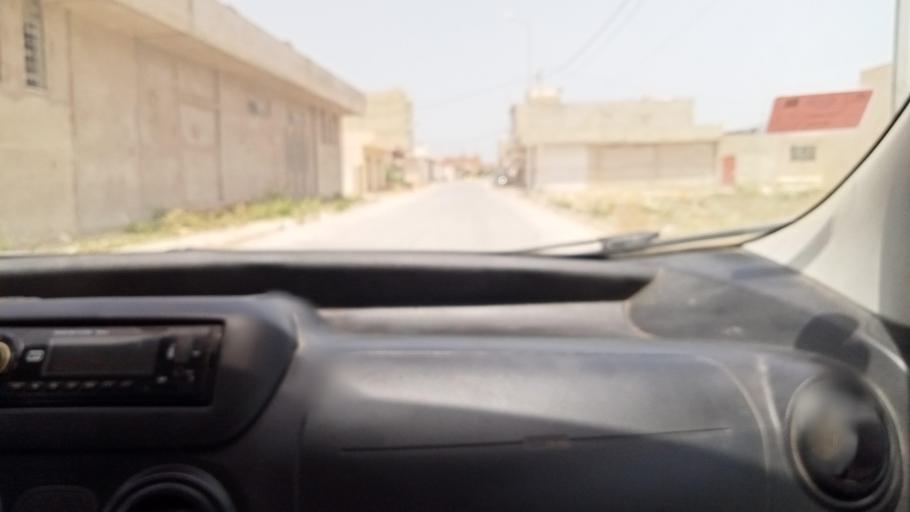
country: TN
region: Nabul
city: Qulaybiyah
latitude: 36.8595
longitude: 11.0887
